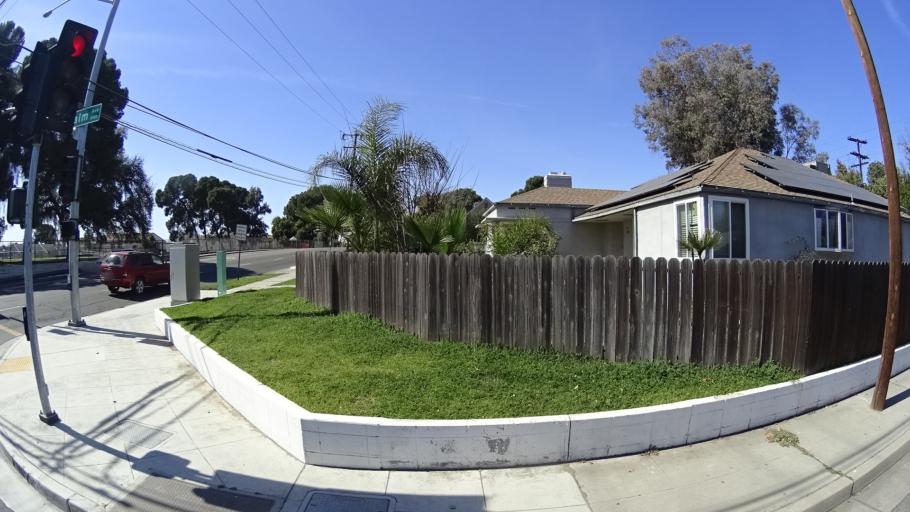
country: US
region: California
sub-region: Fresno County
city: Fresno
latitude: 36.7723
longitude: -119.8087
